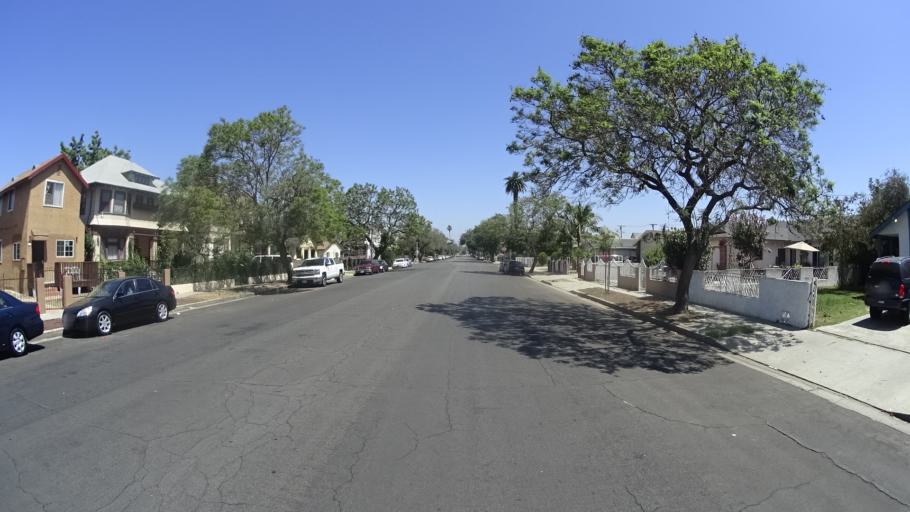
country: US
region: California
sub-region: Los Angeles County
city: View Park-Windsor Hills
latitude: 34.0284
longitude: -118.3015
